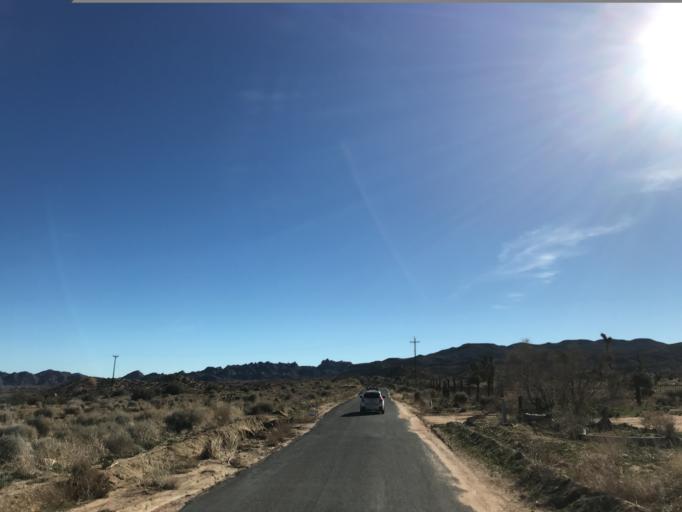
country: US
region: California
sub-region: San Bernardino County
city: Yucca Valley
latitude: 34.1969
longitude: -116.5461
